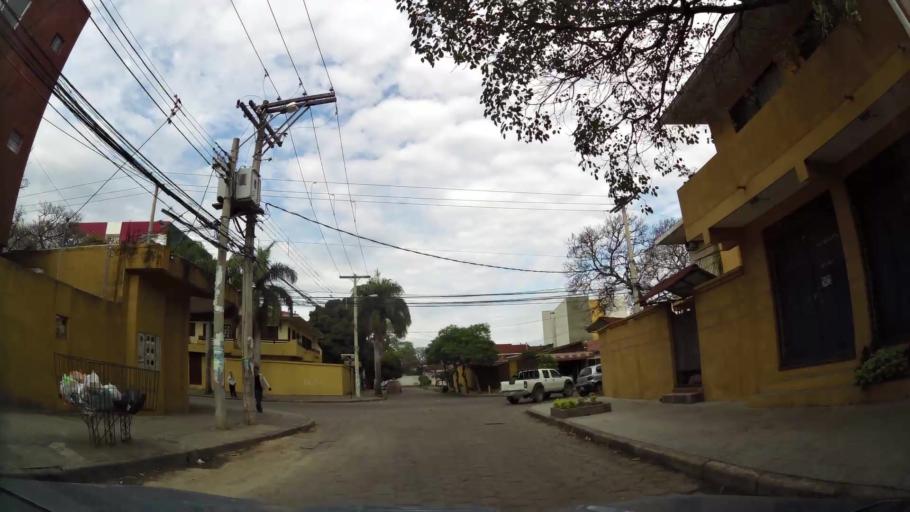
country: BO
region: Santa Cruz
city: Santa Cruz de la Sierra
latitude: -17.7763
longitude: -63.1895
